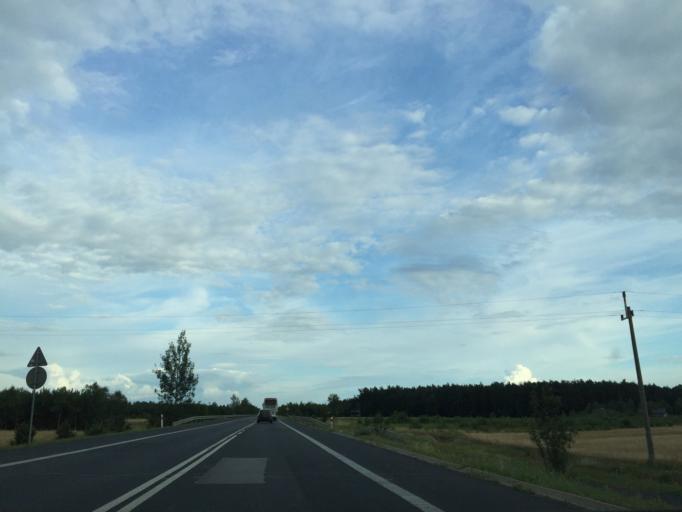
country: PL
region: Lublin Voivodeship
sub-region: Powiat lubartowski
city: Lubartow
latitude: 51.4502
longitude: 22.5801
